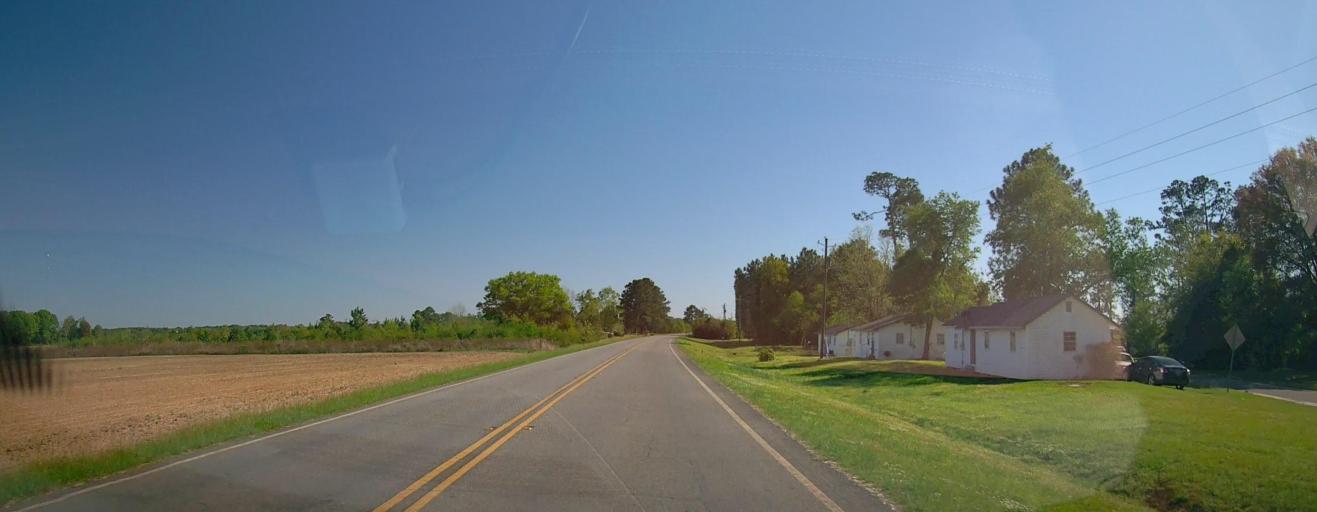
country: US
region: Georgia
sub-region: Wilcox County
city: Rochelle
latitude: 32.1067
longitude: -83.5012
